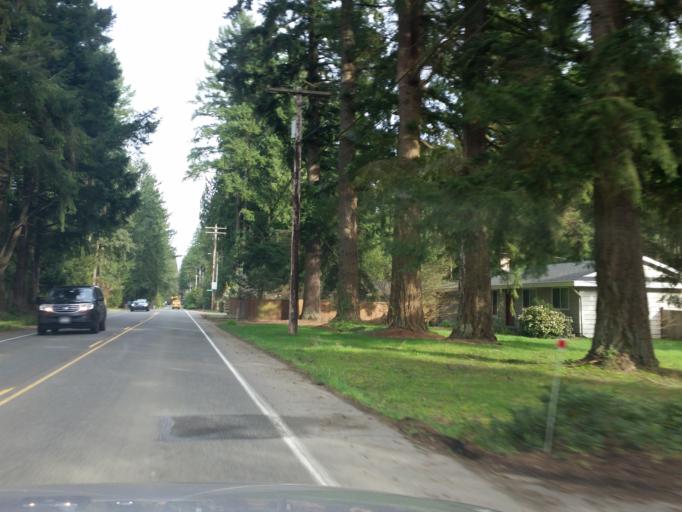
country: US
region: Washington
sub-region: King County
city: Cottage Lake
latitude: 47.7472
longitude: -122.0890
